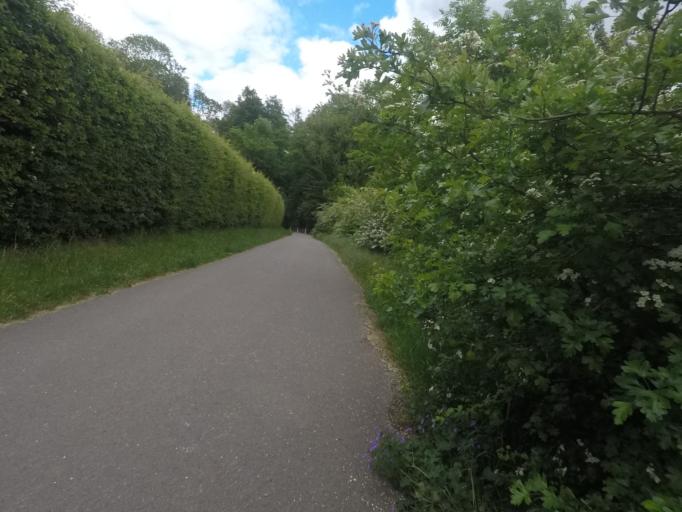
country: DE
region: North Rhine-Westphalia
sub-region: Regierungsbezirk Detmold
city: Bad Salzuflen
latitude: 52.1127
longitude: 8.7157
